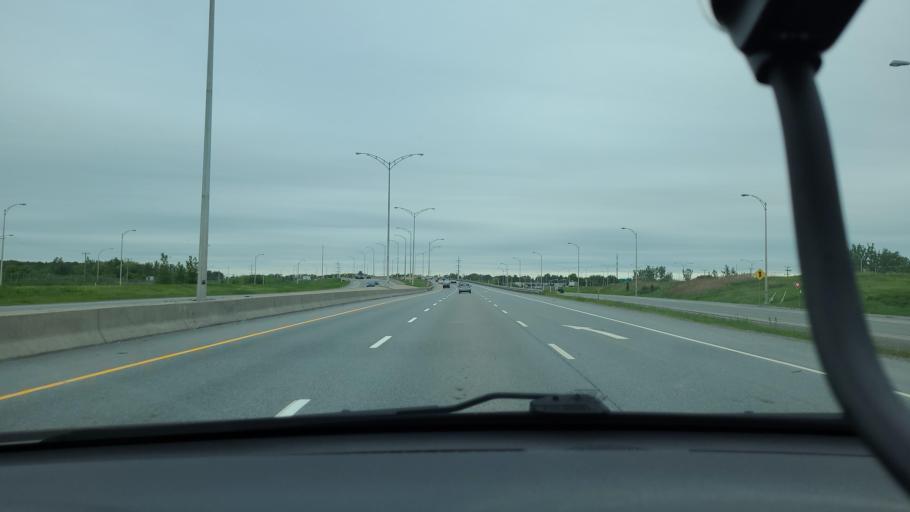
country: CA
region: Quebec
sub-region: Lanaudiere
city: Terrebonne
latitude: 45.6483
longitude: -73.6459
